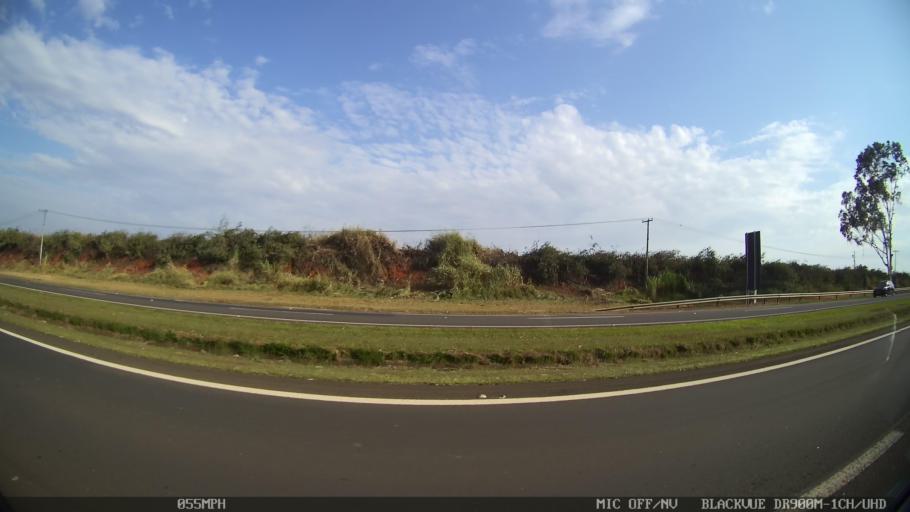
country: BR
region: Sao Paulo
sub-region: Cosmopolis
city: Cosmopolis
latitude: -22.6537
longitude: -47.1849
